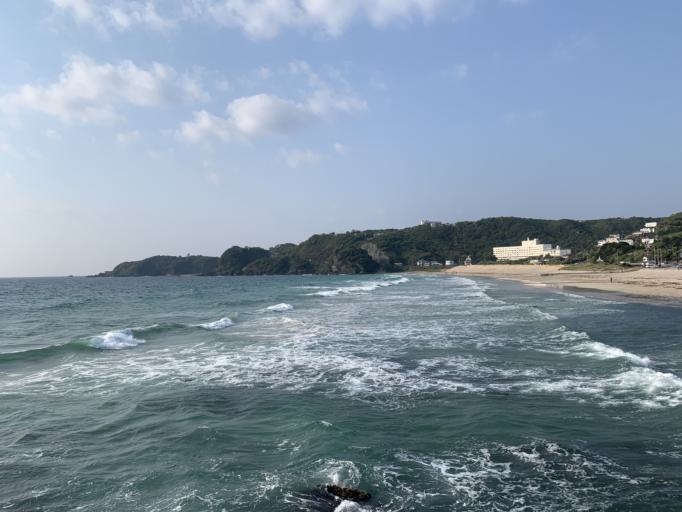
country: JP
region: Shizuoka
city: Shimoda
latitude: 34.6934
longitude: 138.9743
